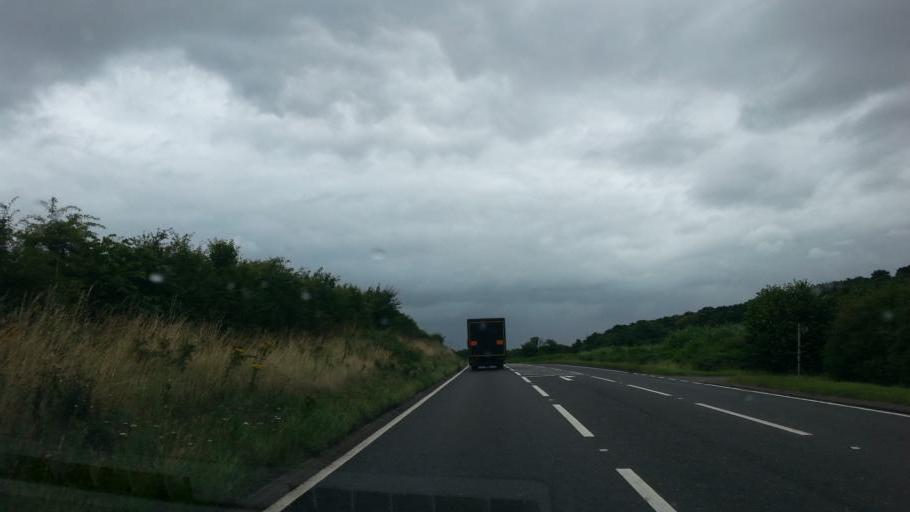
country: GB
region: England
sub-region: Nottinghamshire
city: Bilsthorpe
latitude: 53.1257
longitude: -1.0578
